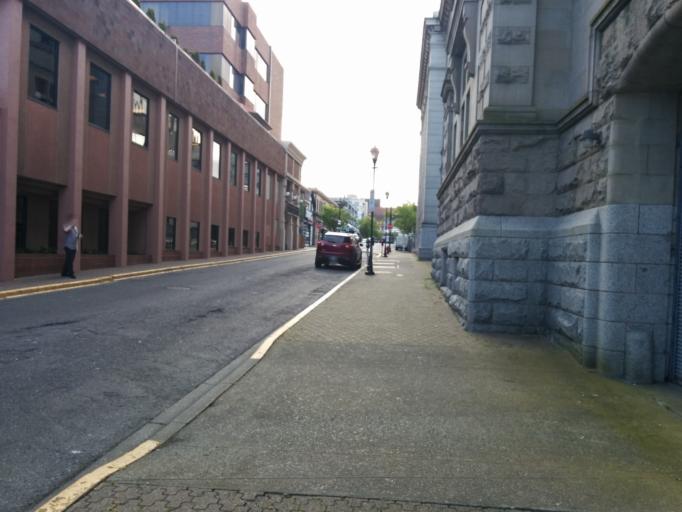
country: CA
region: British Columbia
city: Victoria
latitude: 48.4237
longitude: -123.3694
